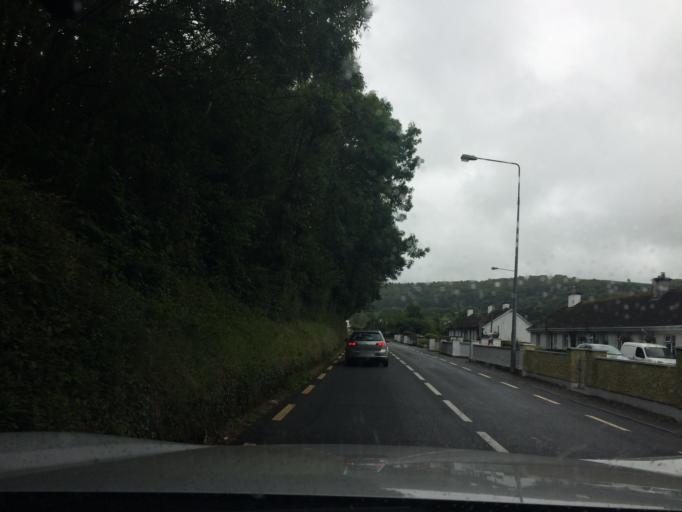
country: IE
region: Munster
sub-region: South Tipperary
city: Cluain Meala
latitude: 52.2700
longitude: -7.7264
